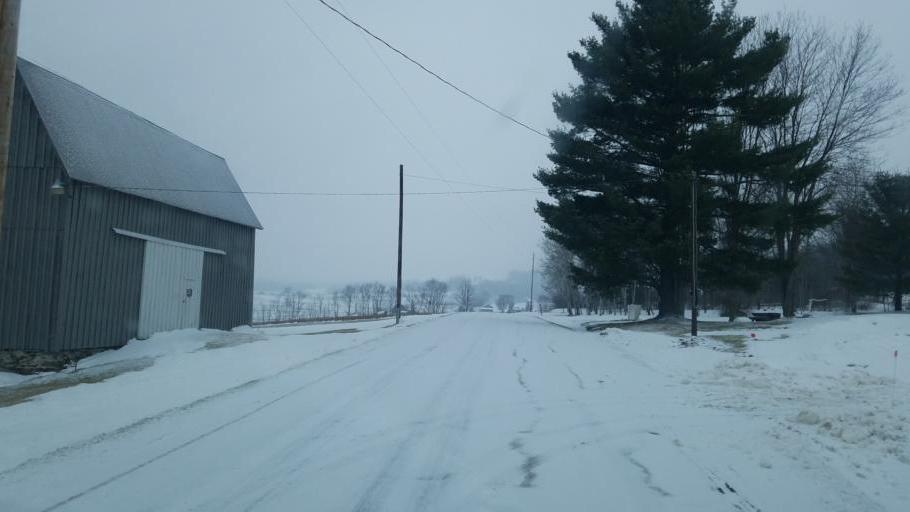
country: US
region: New York
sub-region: Steuben County
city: Canisteo
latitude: 42.1120
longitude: -77.4993
